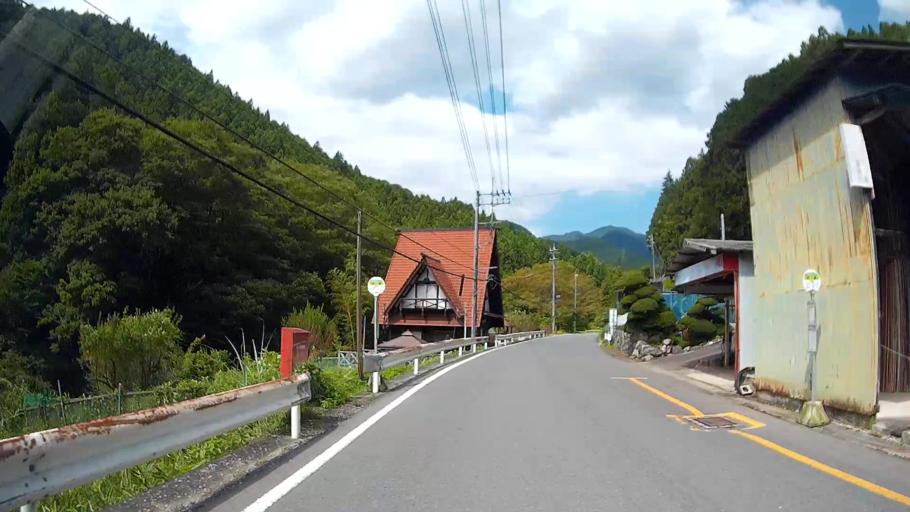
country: JP
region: Saitama
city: Chichibu
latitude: 35.9064
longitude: 139.1562
